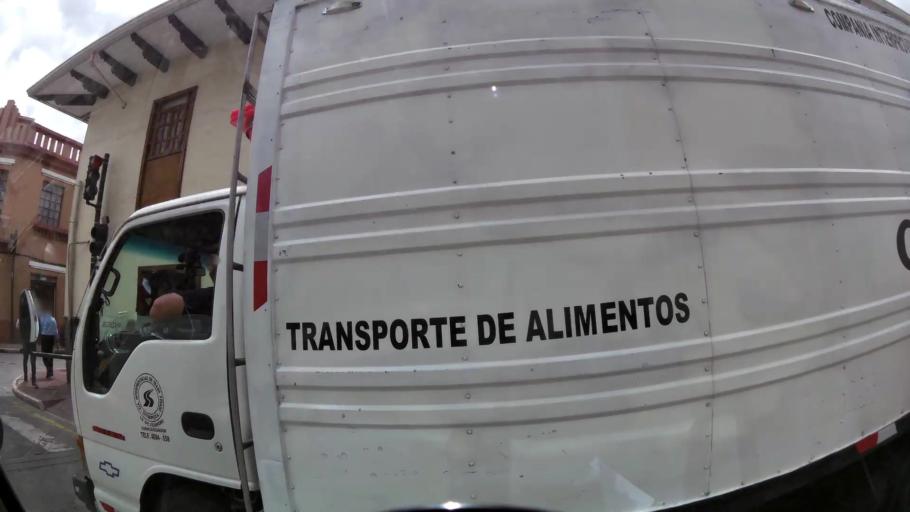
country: EC
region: Azuay
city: Cuenca
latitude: -2.8991
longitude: -79.0033
